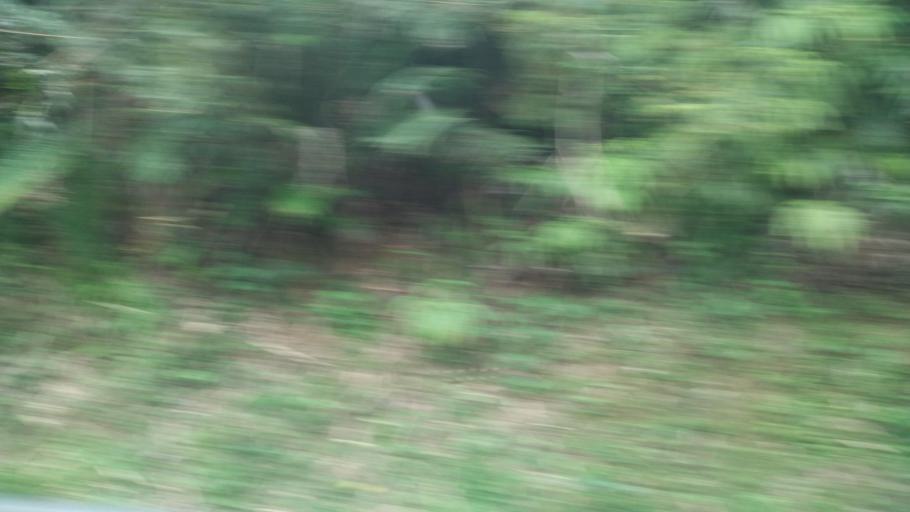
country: TW
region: Taiwan
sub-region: Taoyuan
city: Taoyuan
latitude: 24.9105
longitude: 121.4046
